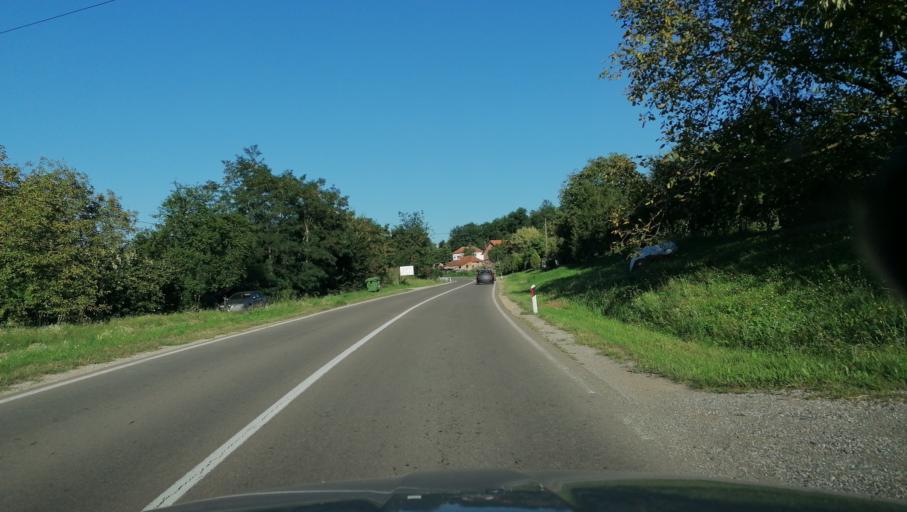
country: RS
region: Central Serbia
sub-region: Sumadijski Okrug
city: Knic
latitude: 43.9265
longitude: 20.6997
